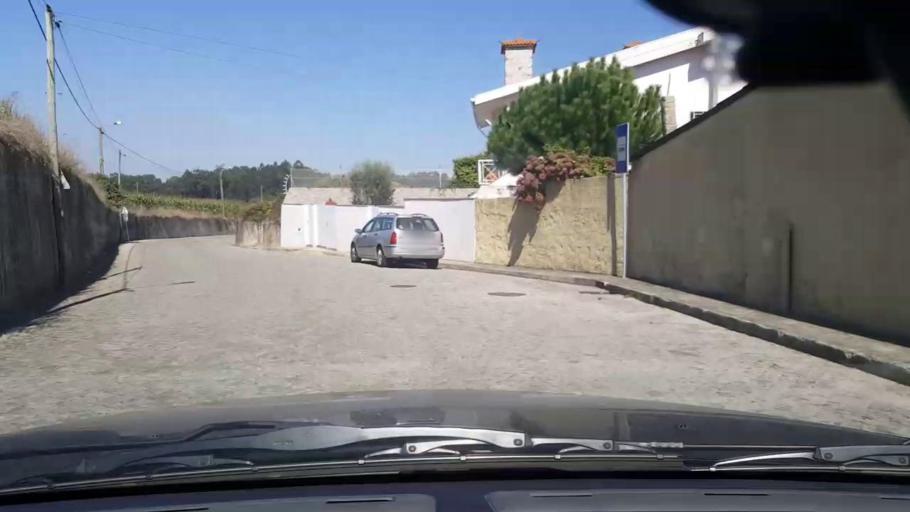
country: PT
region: Porto
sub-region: Matosinhos
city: Lavra
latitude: 41.2684
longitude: -8.6951
